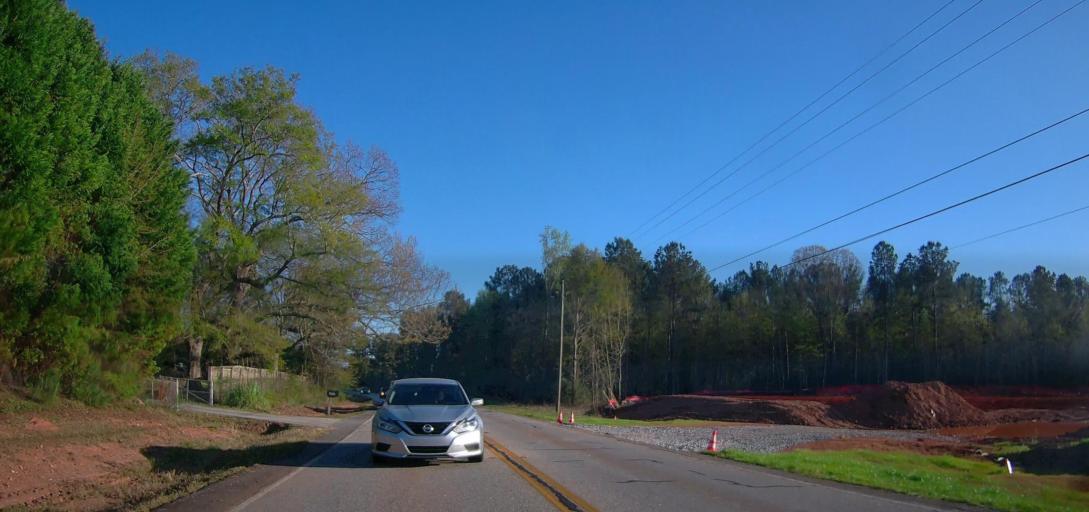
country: US
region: Georgia
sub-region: Newton County
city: Oakwood
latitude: 33.4623
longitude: -83.9071
